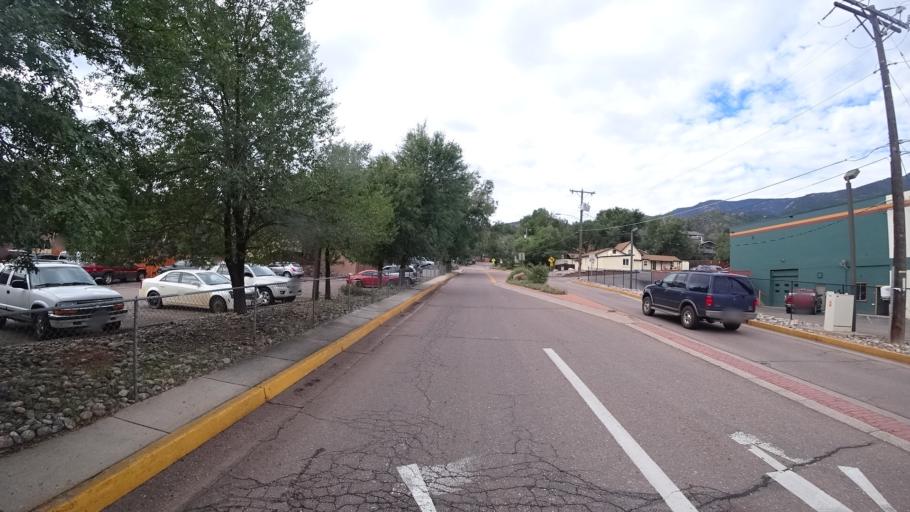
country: US
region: Colorado
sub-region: El Paso County
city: Manitou Springs
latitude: 38.8565
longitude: -104.8987
